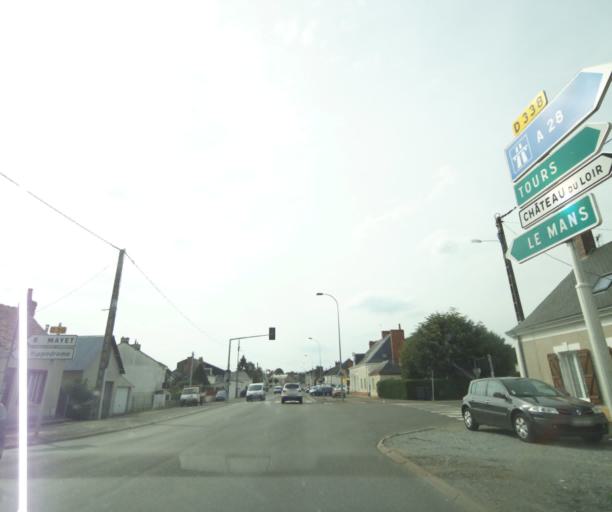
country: FR
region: Pays de la Loire
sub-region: Departement de la Sarthe
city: Ecommoy
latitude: 47.8265
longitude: 0.2829
